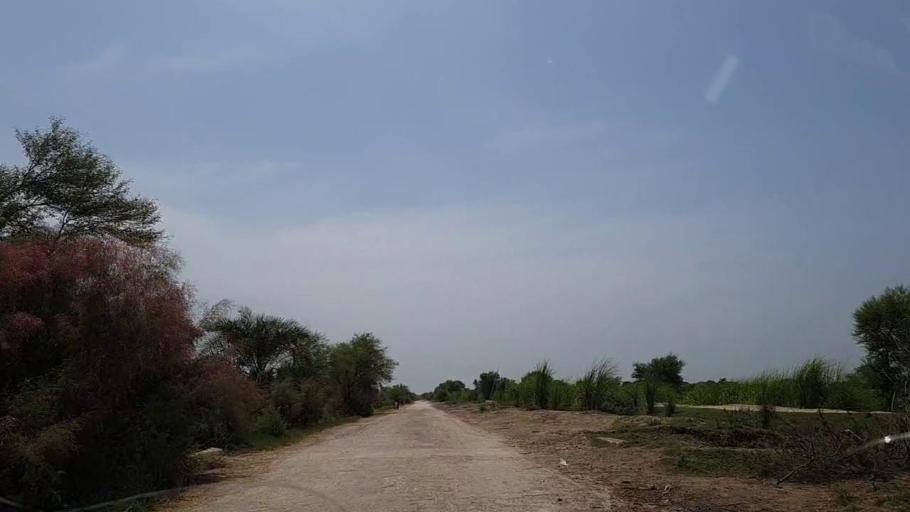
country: PK
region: Sindh
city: Khanpur
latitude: 27.8485
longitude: 69.4855
